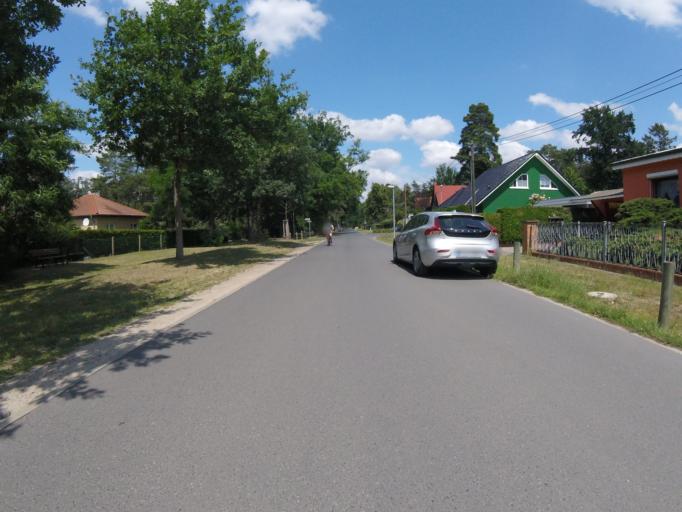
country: DE
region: Brandenburg
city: Bestensee
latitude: 52.2764
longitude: 13.6574
